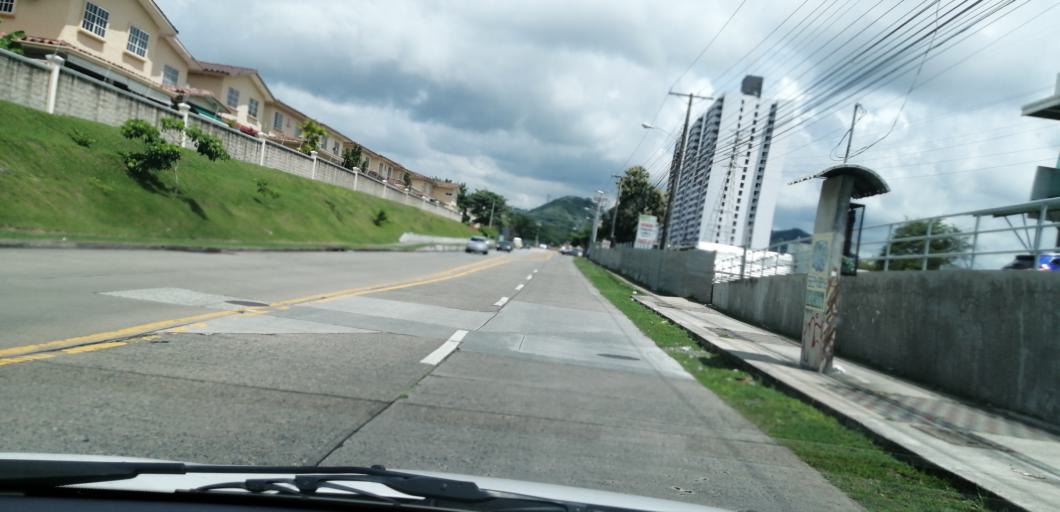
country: PA
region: Panama
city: Panama
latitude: 9.0323
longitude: -79.5267
